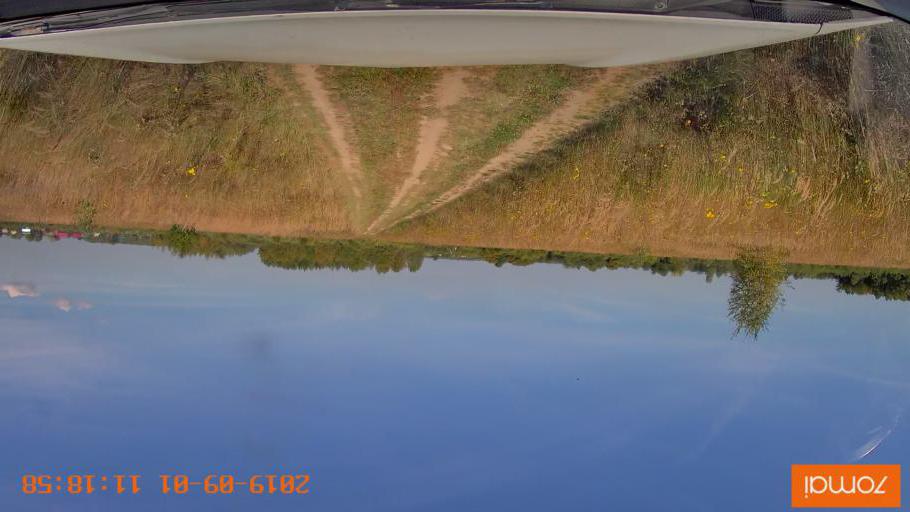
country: RU
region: Kaluga
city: Detchino
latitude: 54.8272
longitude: 36.3639
